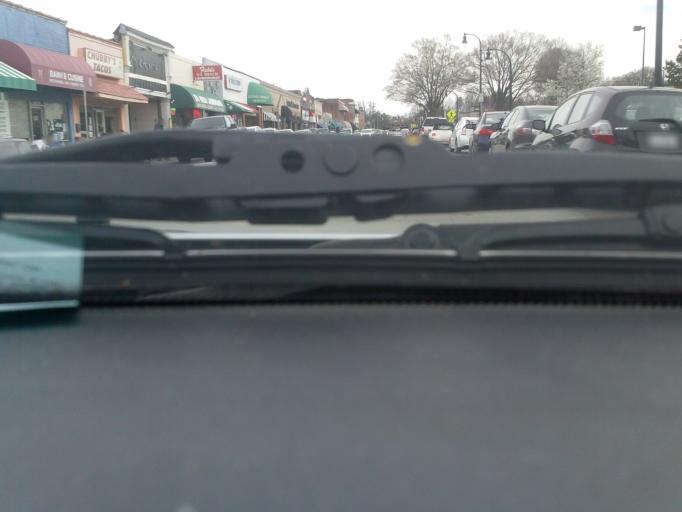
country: US
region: North Carolina
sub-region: Durham County
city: Durham
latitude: 36.0097
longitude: -78.9221
